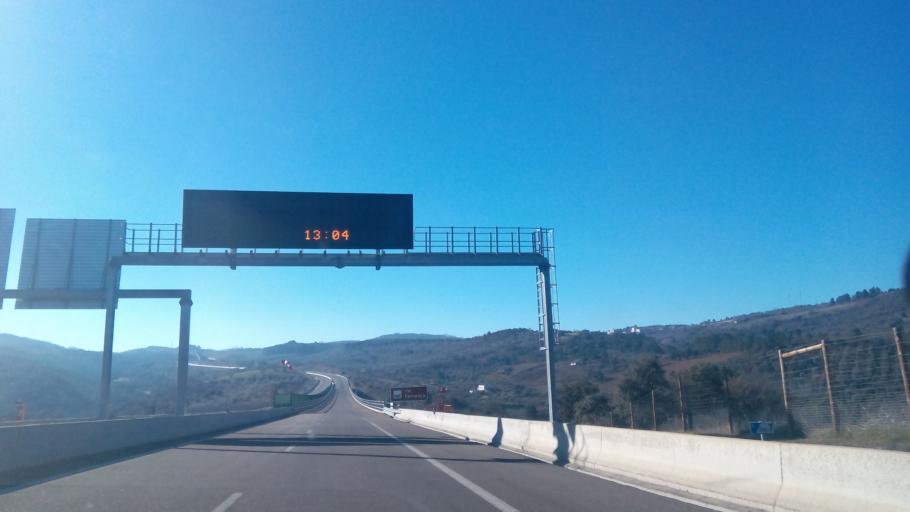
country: PT
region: Braganca
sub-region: Braganca Municipality
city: Braganca
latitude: 41.7901
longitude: -6.7266
